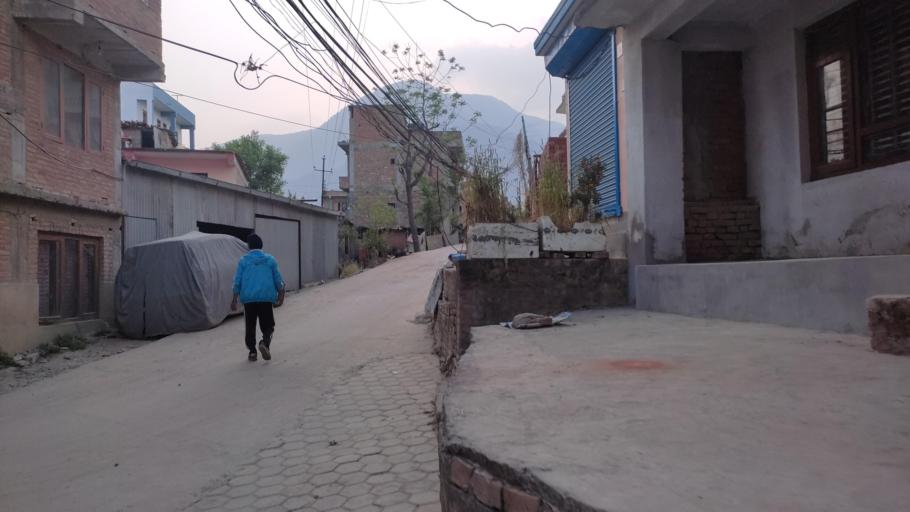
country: NP
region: Central Region
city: Kirtipur
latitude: 27.6684
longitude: 85.2734
